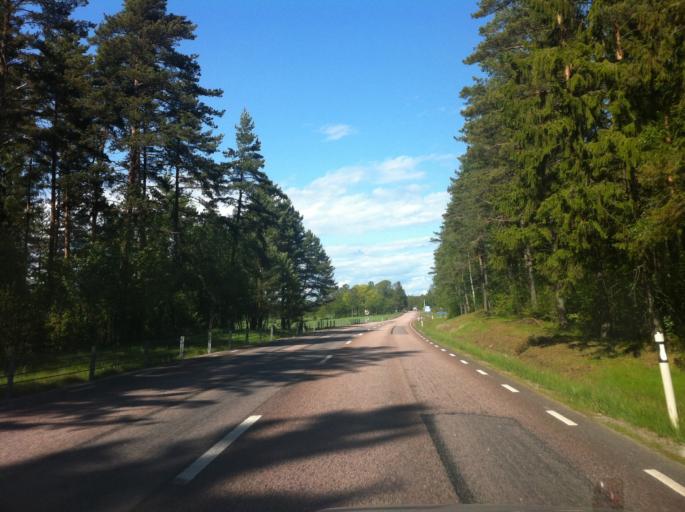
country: SE
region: Vaestra Goetaland
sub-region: Gullspangs Kommun
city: Gullspang
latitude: 59.0835
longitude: 14.1580
